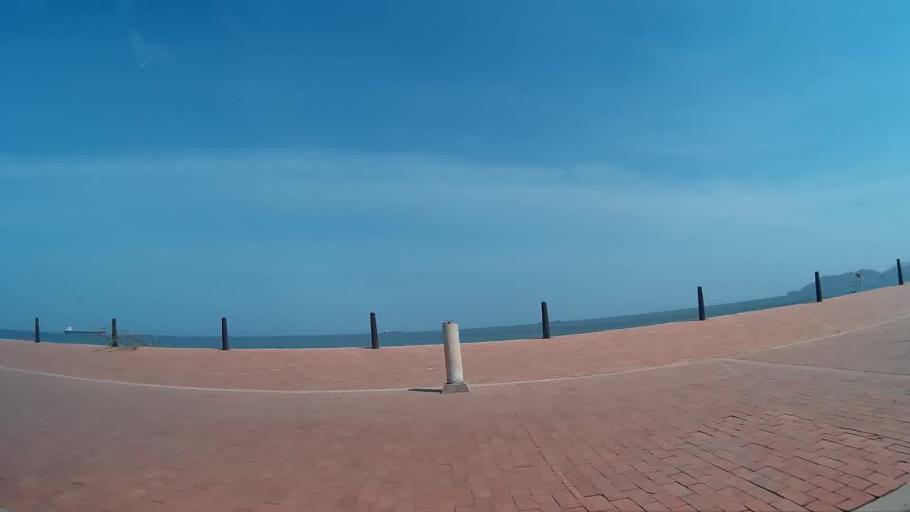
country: CO
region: Magdalena
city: Santa Marta
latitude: 11.1279
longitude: -74.2311
